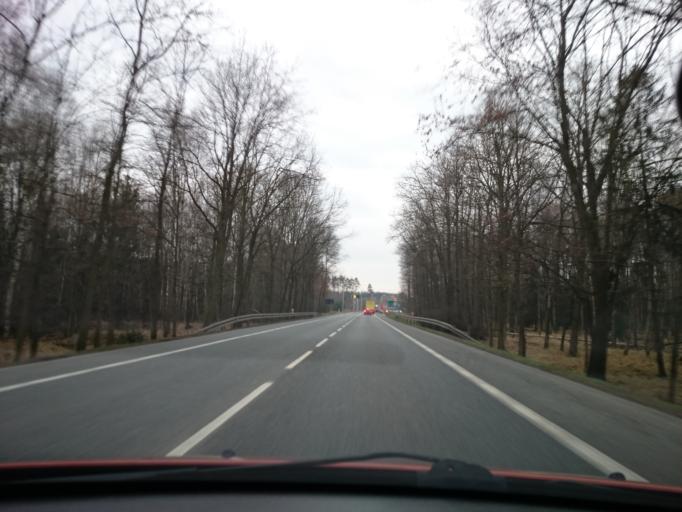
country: PL
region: Opole Voivodeship
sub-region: Powiat opolski
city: Dabrowa
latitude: 50.6691
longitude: 17.7032
